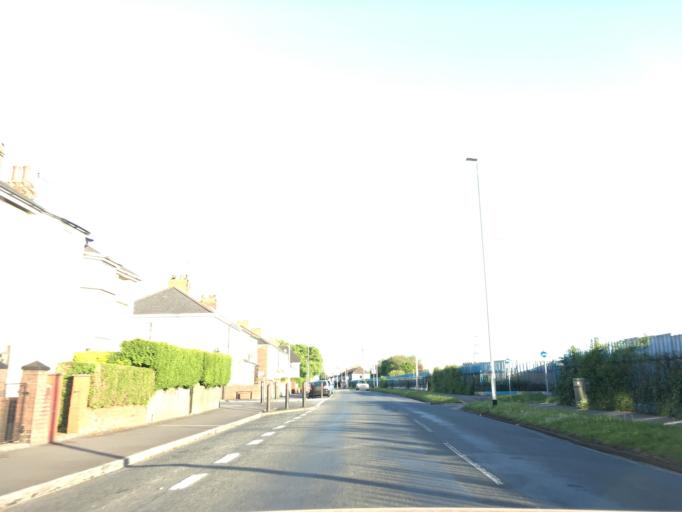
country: GB
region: Wales
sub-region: Newport
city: Newport
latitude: 51.5760
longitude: -2.9970
